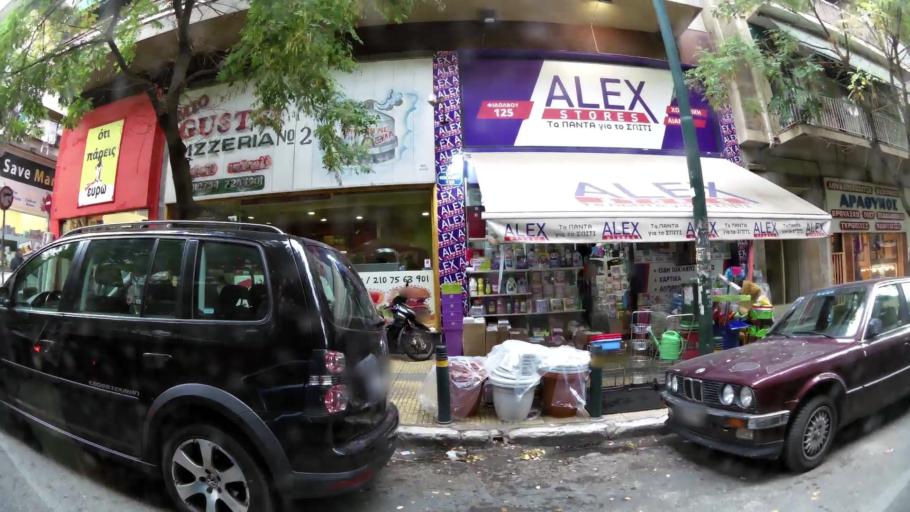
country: GR
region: Attica
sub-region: Nomarchia Athinas
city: Vyronas
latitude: 37.9625
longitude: 23.7451
